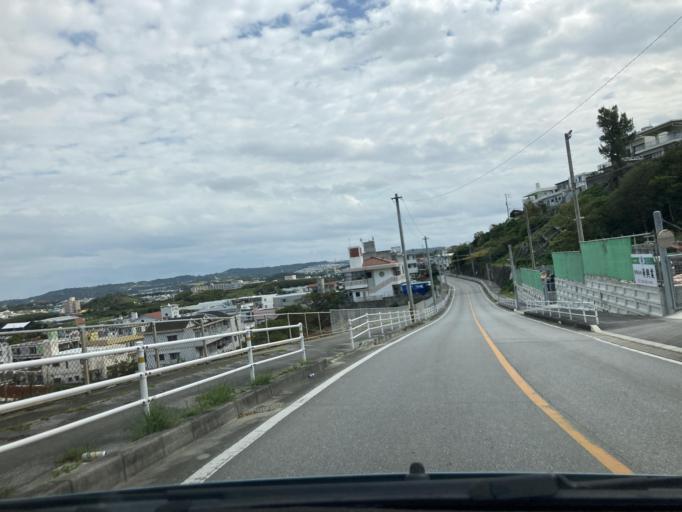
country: JP
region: Okinawa
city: Tomigusuku
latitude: 26.1800
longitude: 127.7040
